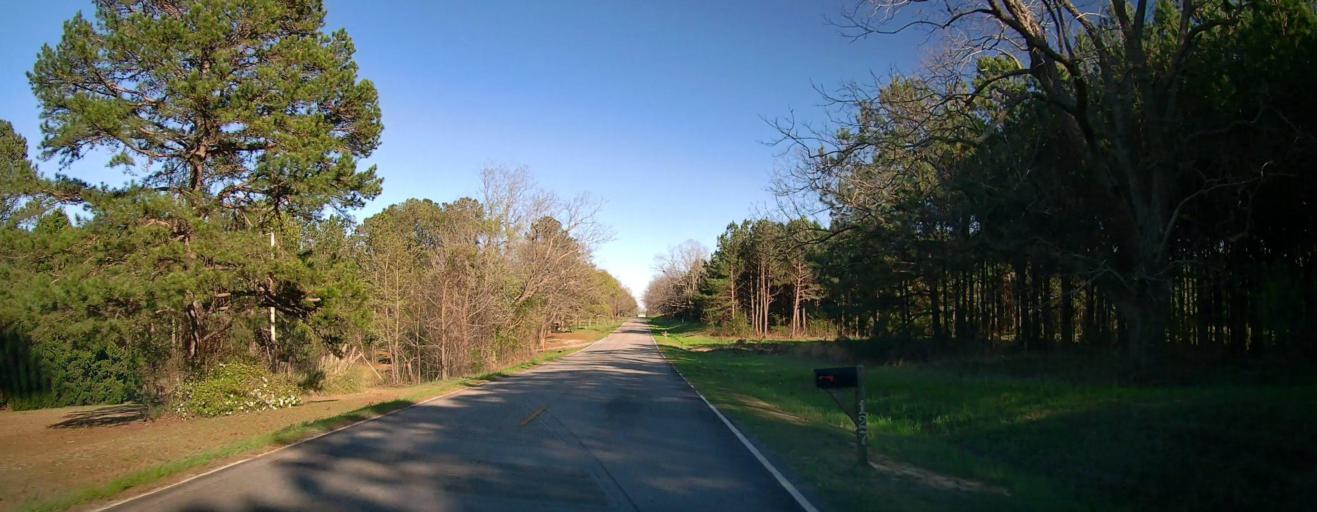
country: US
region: Georgia
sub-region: Houston County
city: Perry
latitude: 32.3745
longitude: -83.7168
